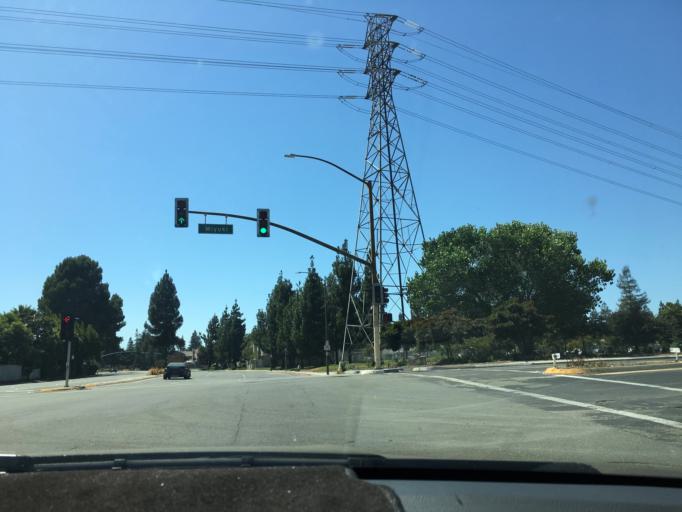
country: US
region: California
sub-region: Santa Clara County
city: Seven Trees
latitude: 37.2366
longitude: -121.7933
